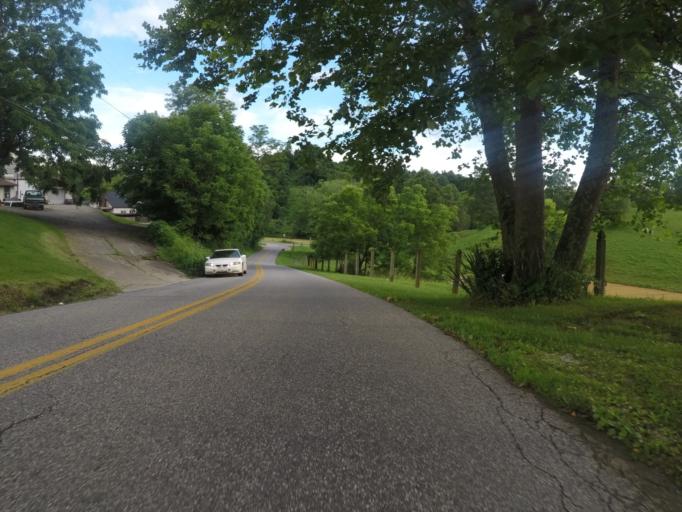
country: US
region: West Virginia
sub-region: Cabell County
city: Pea Ridge
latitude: 38.3880
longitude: -82.3619
